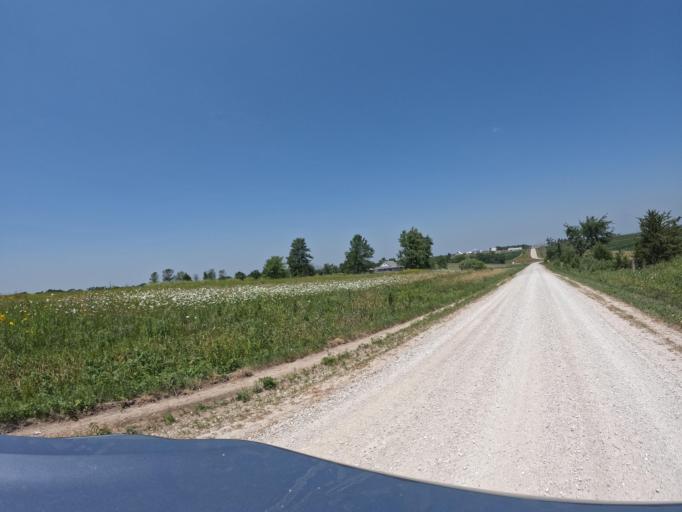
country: US
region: Iowa
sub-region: Keokuk County
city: Sigourney
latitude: 41.2735
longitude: -92.1806
